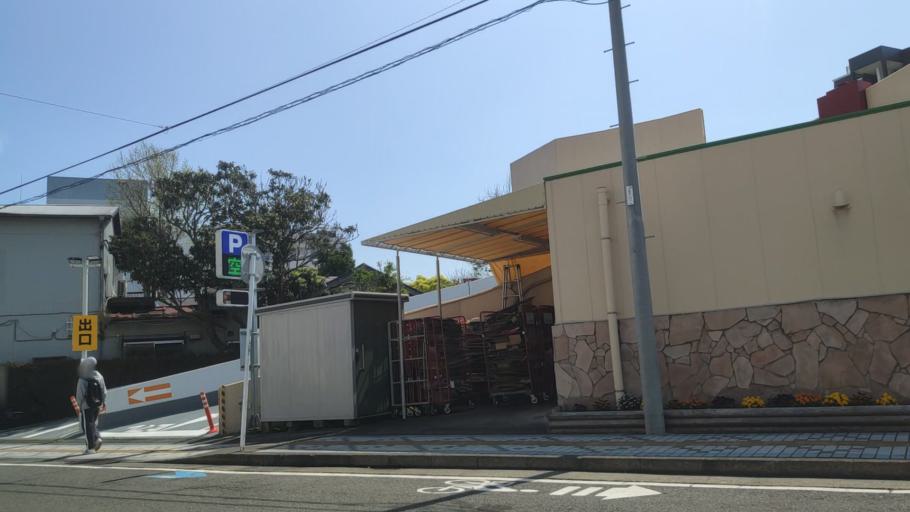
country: JP
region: Kanagawa
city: Hiratsuka
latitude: 35.3262
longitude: 139.3497
